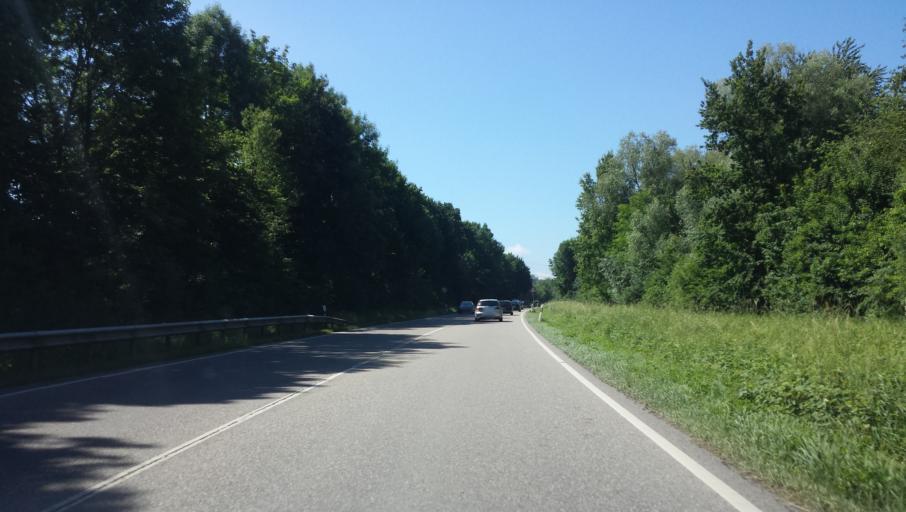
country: DE
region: Baden-Wuerttemberg
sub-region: Karlsruhe Region
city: Nussloch
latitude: 49.3137
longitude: 8.6836
